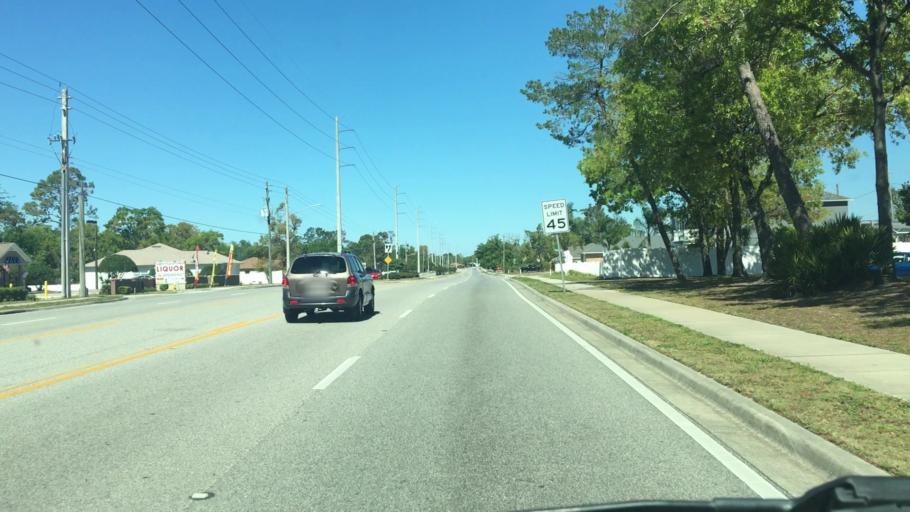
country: US
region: Florida
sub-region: Volusia County
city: Deltona
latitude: 28.9035
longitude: -81.1726
